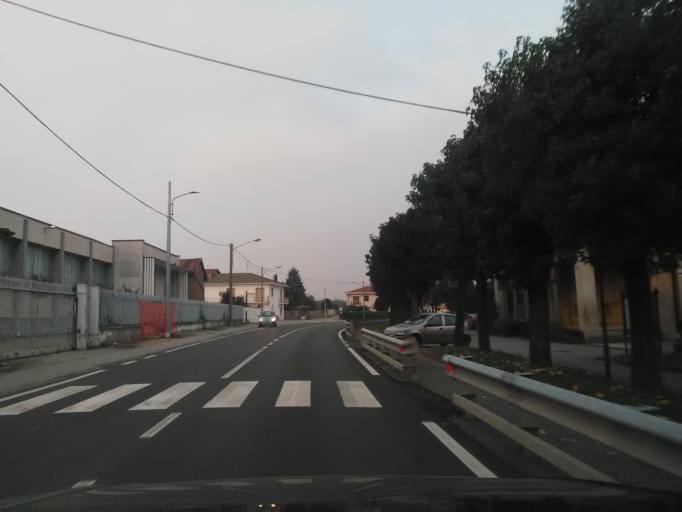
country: IT
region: Piedmont
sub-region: Provincia di Vercelli
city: Borgo d'Ale
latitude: 45.3546
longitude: 8.0579
